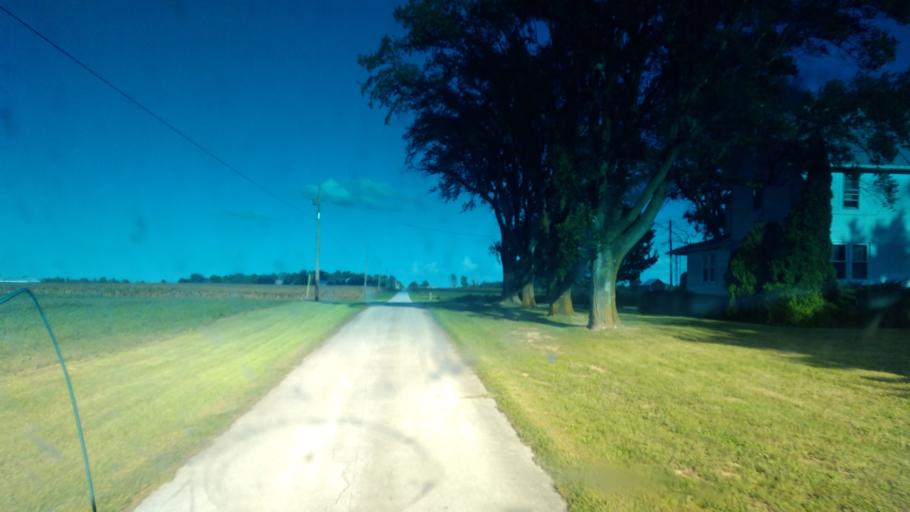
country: US
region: Ohio
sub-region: Wyandot County
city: Carey
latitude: 40.9411
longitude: -83.4736
